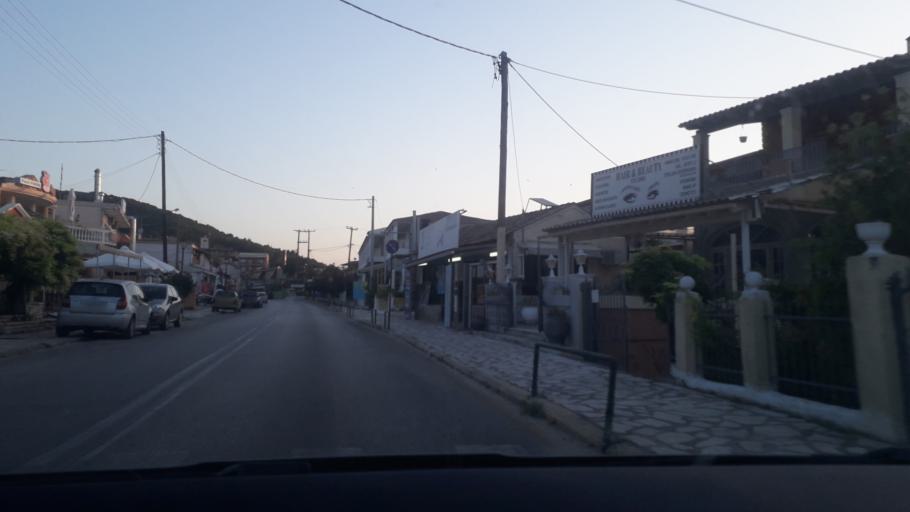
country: GR
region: Ionian Islands
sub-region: Nomos Kerkyras
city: Agios Matthaios
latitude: 39.4836
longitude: 19.9249
